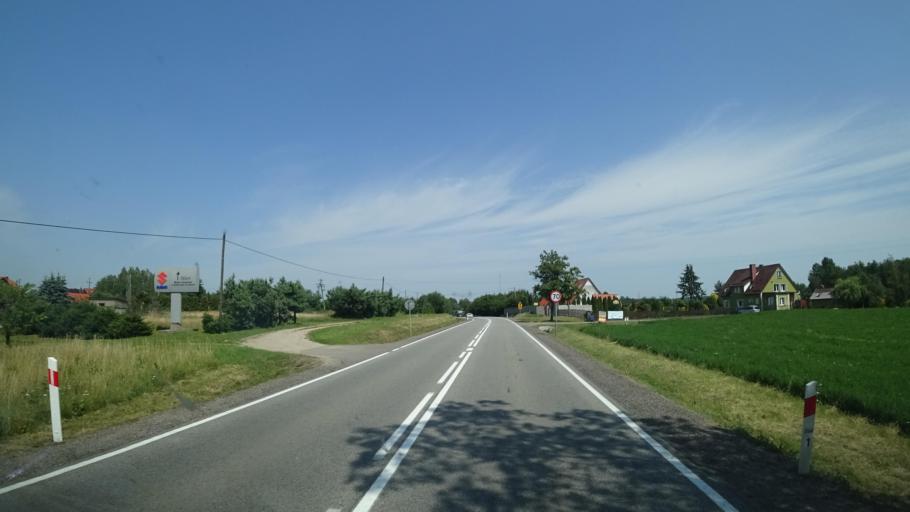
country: PL
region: Pomeranian Voivodeship
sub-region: Powiat koscierski
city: Koscierzyna
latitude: 54.1435
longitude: 18.0230
